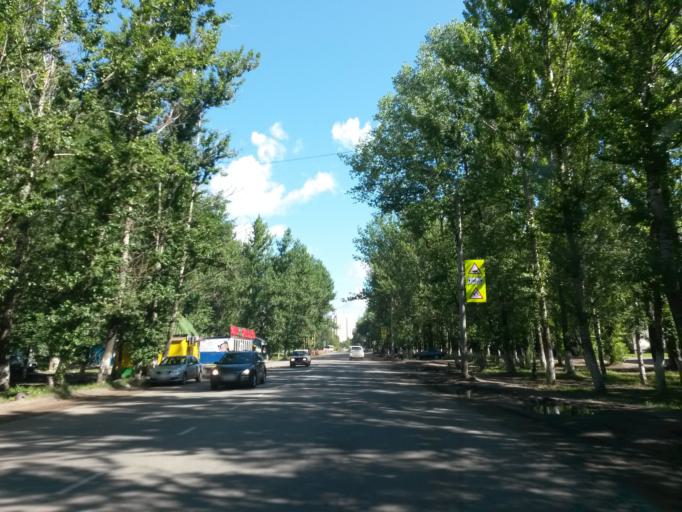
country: RU
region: Jaroslavl
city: Yaroslavl
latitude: 57.5721
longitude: 39.8604
